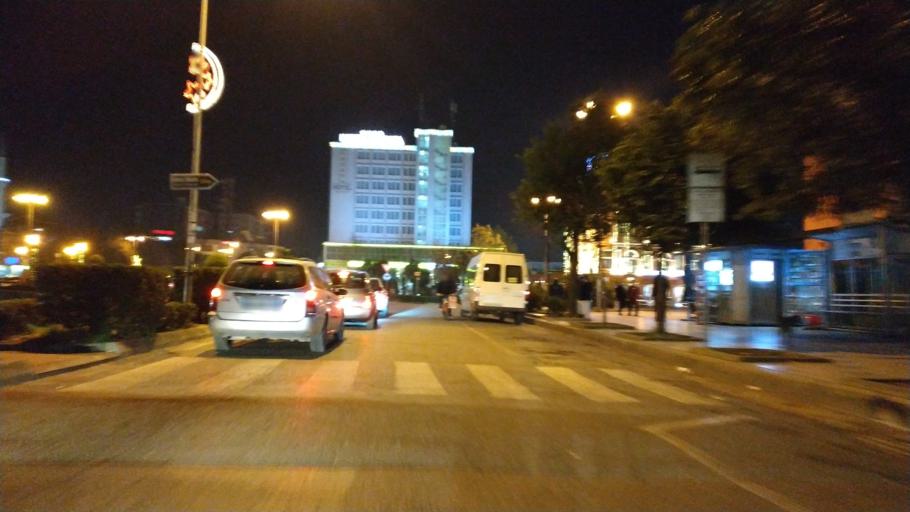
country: AL
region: Shkoder
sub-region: Rrethi i Shkodres
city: Shkoder
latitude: 42.0682
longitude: 19.5112
